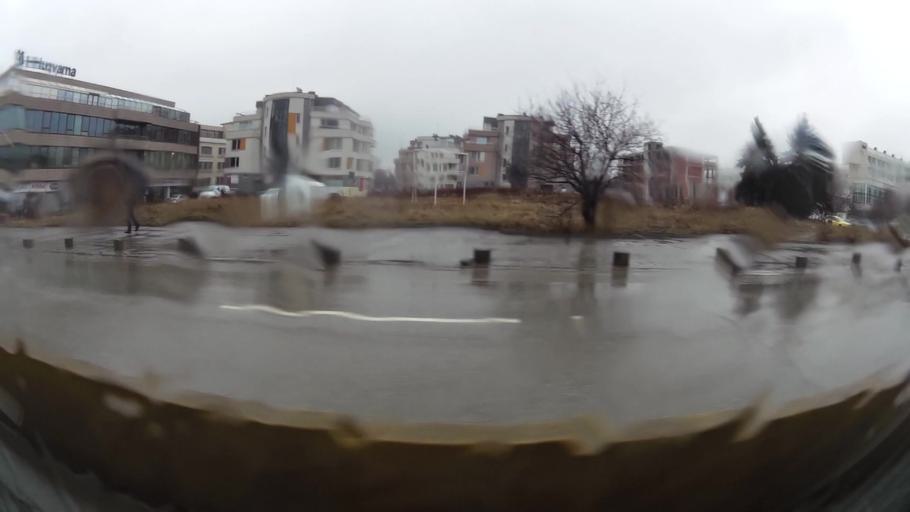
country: BG
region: Sofia-Capital
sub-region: Stolichna Obshtina
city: Sofia
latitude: 42.6518
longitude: 23.3511
